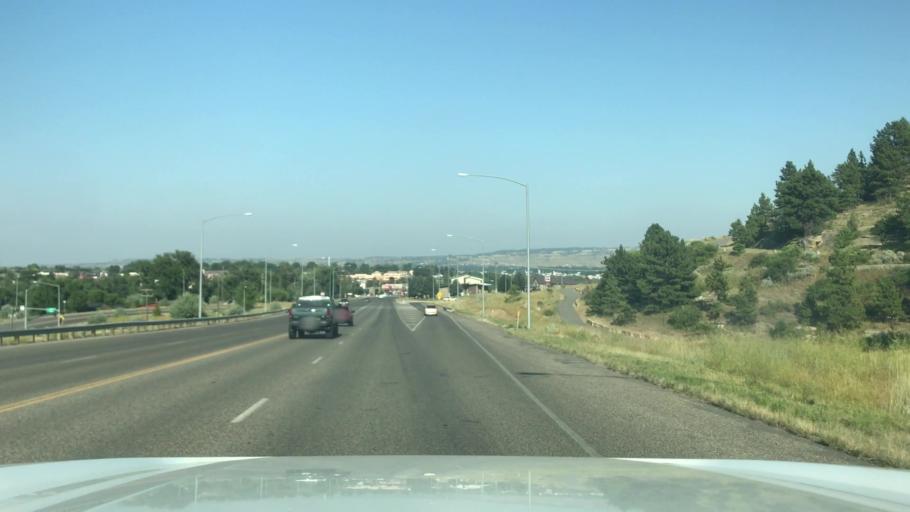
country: US
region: Montana
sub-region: Yellowstone County
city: Billings
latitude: 45.8027
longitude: -108.4861
